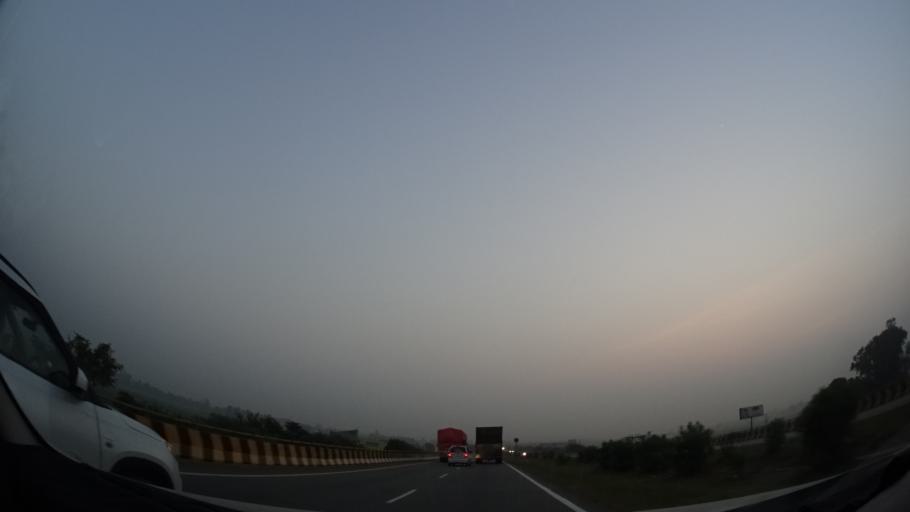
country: IN
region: Uttar Pradesh
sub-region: Bara Banki
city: Nawabganj
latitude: 26.9208
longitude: 81.2225
